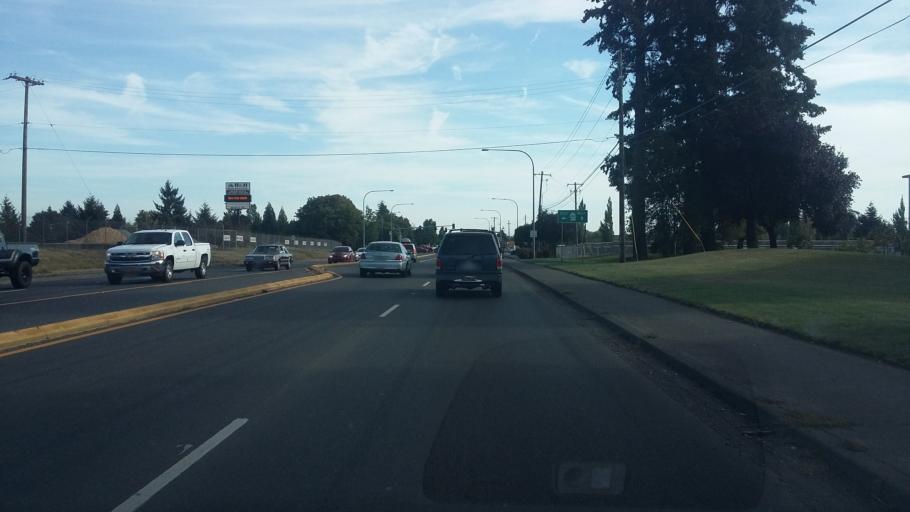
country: US
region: Washington
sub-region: Clark County
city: Orchards
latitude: 45.6842
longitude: -122.5527
